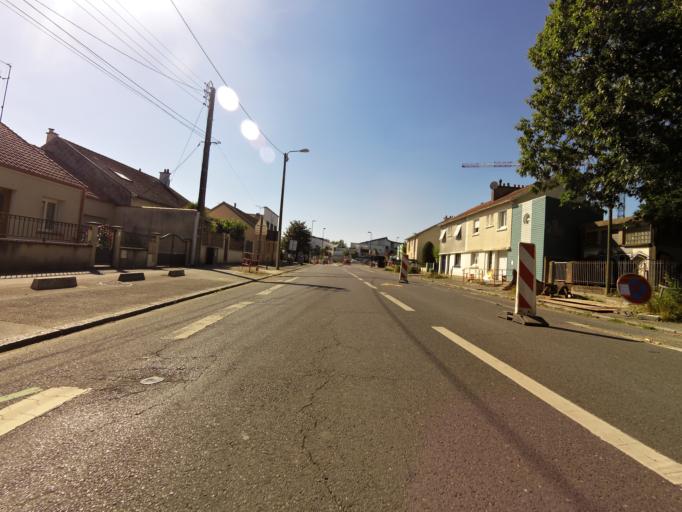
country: FR
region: Pays de la Loire
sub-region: Departement de la Loire-Atlantique
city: Nantes
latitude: 47.2527
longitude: -1.5751
